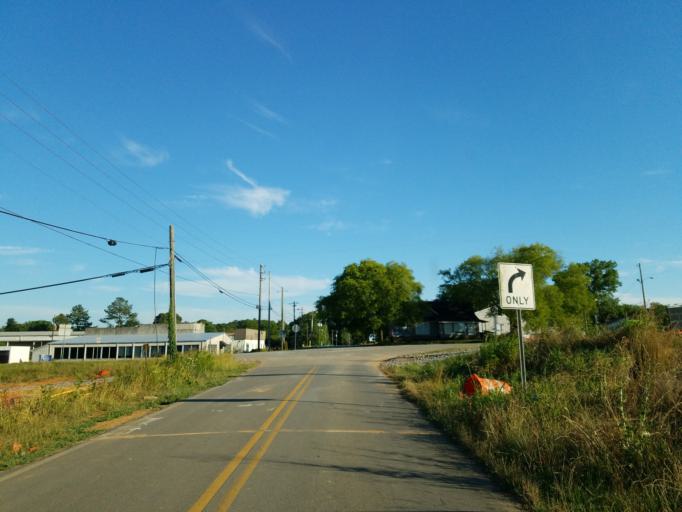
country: US
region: Georgia
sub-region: Bartow County
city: Adairsville
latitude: 34.3775
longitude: -84.9352
